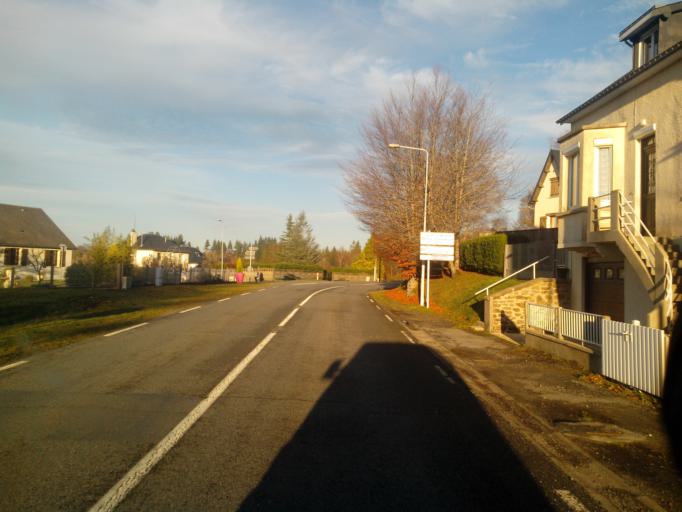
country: FR
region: Limousin
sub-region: Departement de la Correze
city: Bugeat
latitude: 45.5967
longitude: 1.9386
